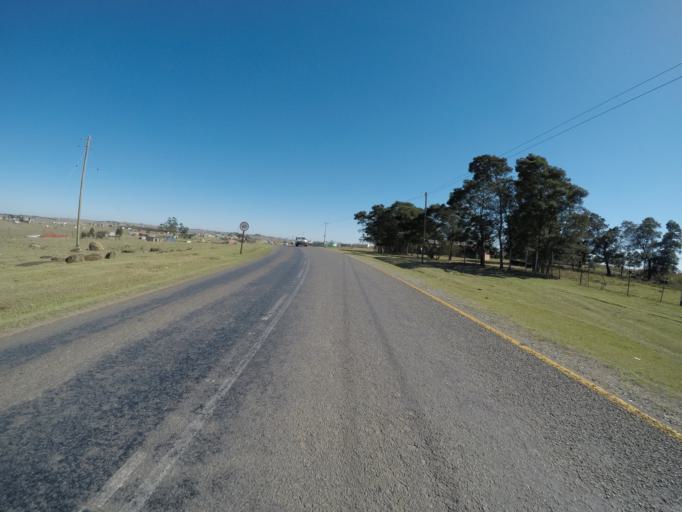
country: ZA
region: Eastern Cape
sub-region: OR Tambo District Municipality
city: Mthatha
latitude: -31.7911
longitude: 28.7451
